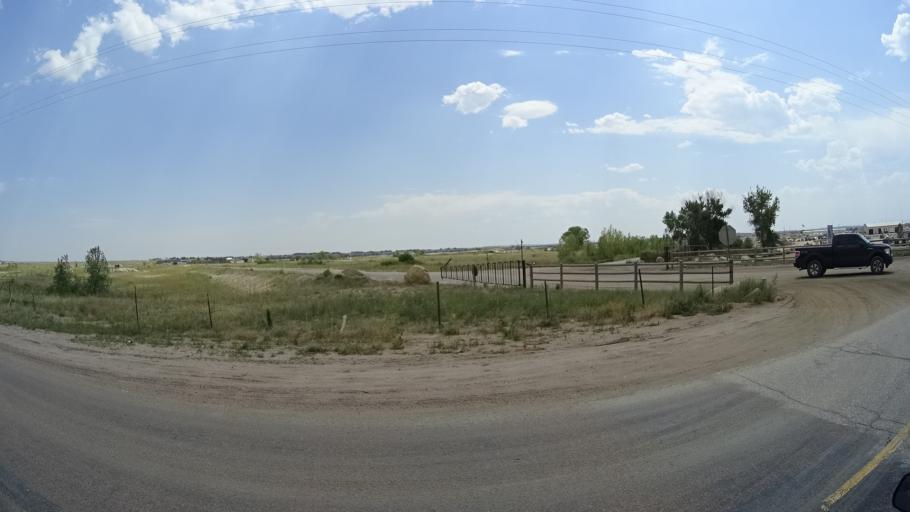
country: US
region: Colorado
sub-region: El Paso County
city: Black Forest
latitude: 38.9552
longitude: -104.6882
